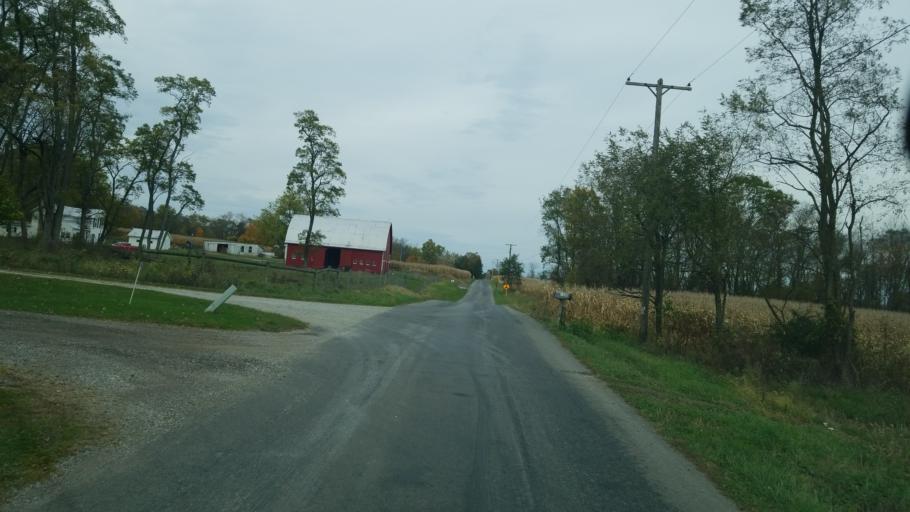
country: US
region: Ohio
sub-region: Ashland County
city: Ashland
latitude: 40.8712
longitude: -82.2403
